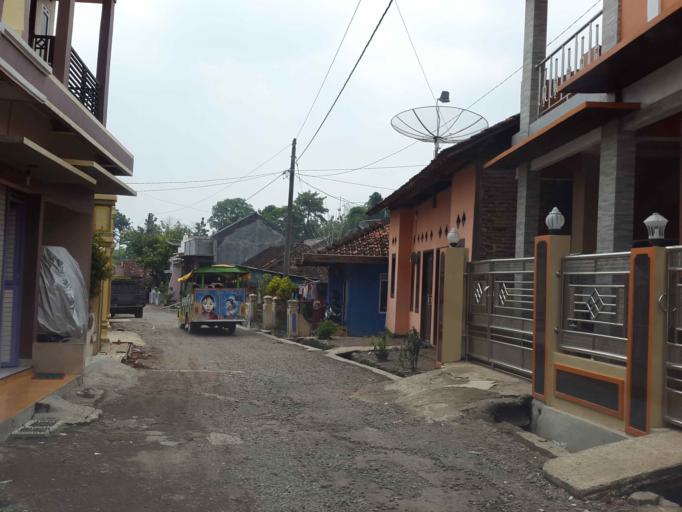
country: ID
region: Central Java
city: Pamedaran
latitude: -7.0680
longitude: 108.8652
